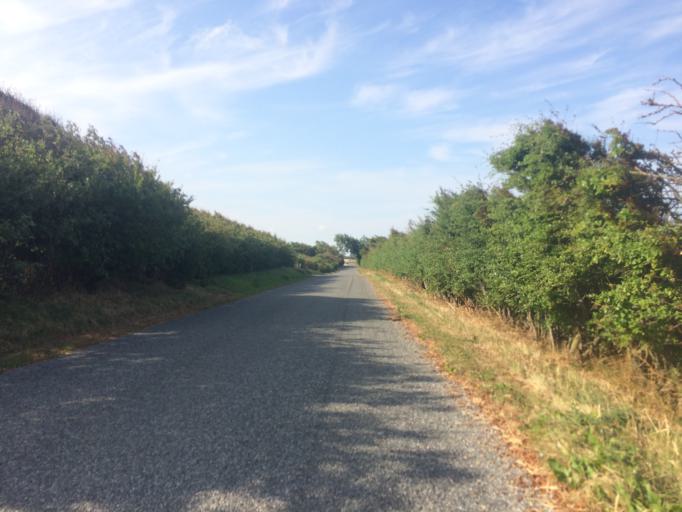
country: DK
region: North Denmark
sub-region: Morso Kommune
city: Nykobing Mors
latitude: 56.6449
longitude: 8.7833
